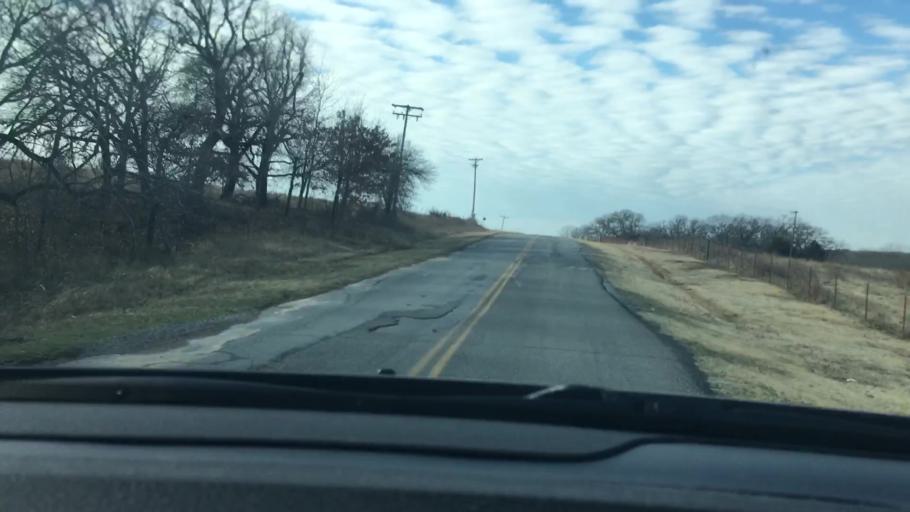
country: US
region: Oklahoma
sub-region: Garvin County
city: Pauls Valley
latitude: 34.7386
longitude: -97.1408
